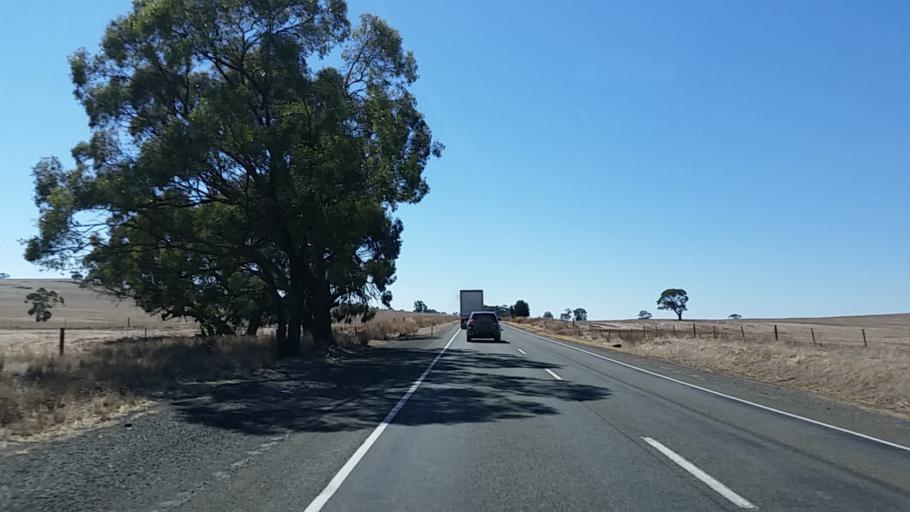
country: AU
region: South Australia
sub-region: Clare and Gilbert Valleys
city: Clare
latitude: -34.0461
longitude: 138.7986
